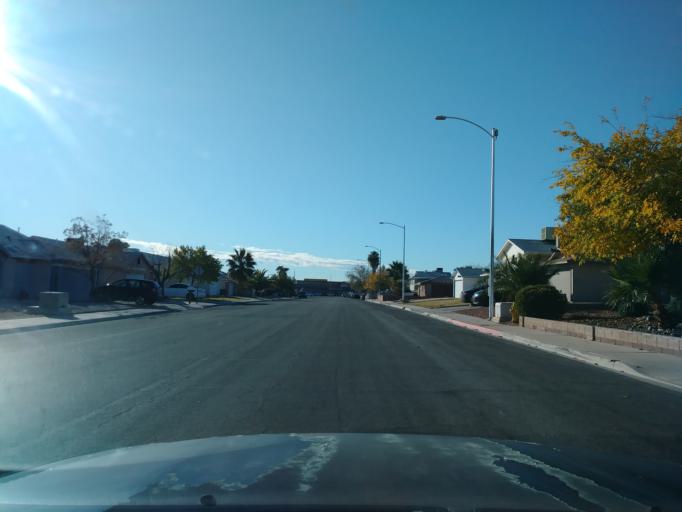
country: US
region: Nevada
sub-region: Clark County
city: Spring Valley
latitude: 36.1612
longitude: -115.2465
